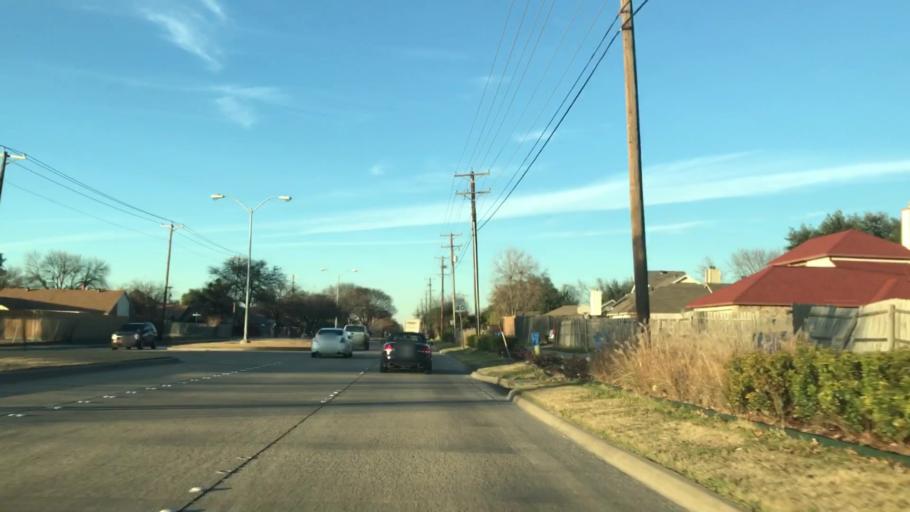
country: US
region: Texas
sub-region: Dallas County
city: Rowlett
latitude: 32.9076
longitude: -96.5179
